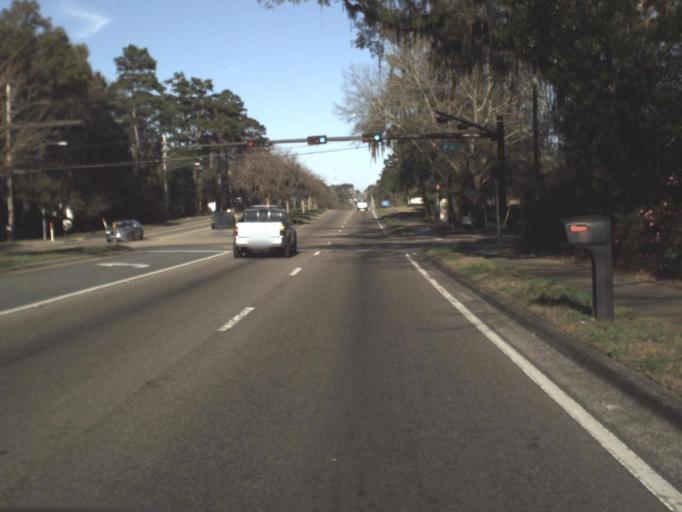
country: US
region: Florida
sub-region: Leon County
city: Tallahassee
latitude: 30.4542
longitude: -84.2441
